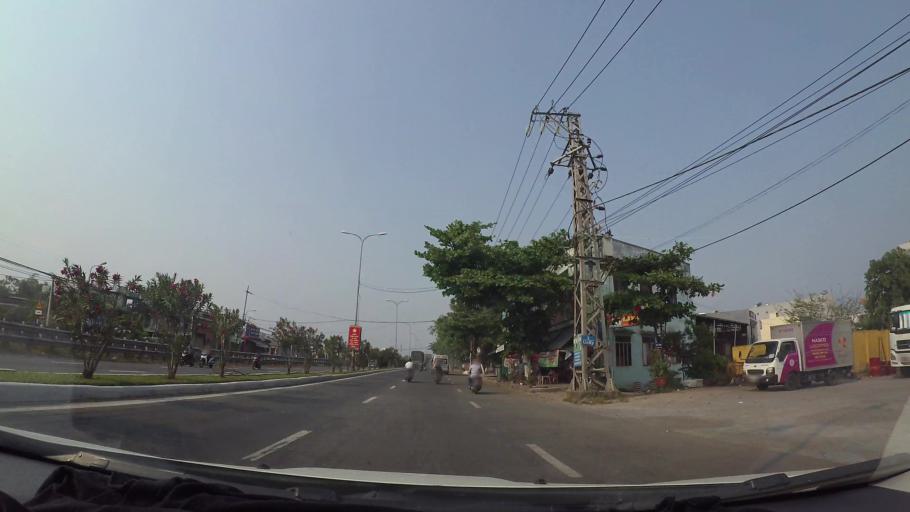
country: VN
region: Da Nang
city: Cam Le
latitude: 16.0165
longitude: 108.1933
